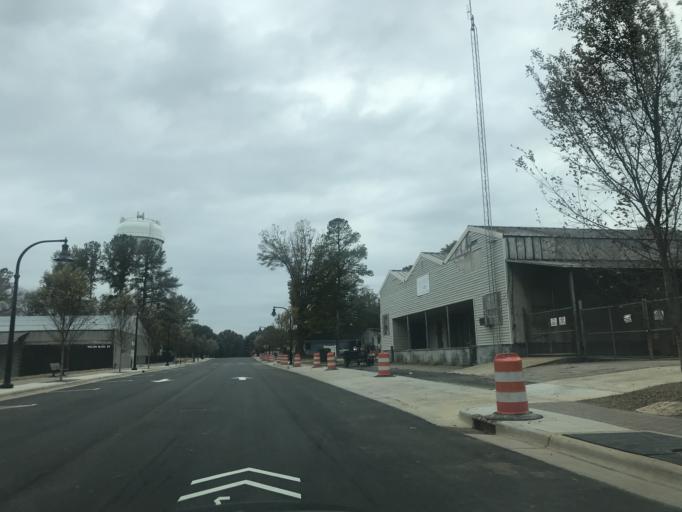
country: US
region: North Carolina
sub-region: Wake County
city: Wake Forest
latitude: 35.9735
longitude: -78.5117
